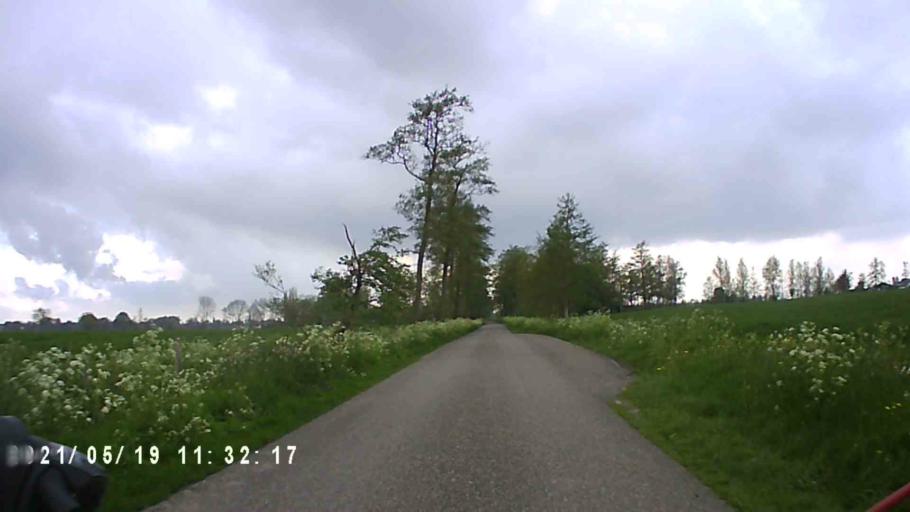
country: NL
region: Friesland
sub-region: Gemeente Kollumerland en Nieuwkruisland
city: Kollum
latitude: 53.2762
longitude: 6.1709
